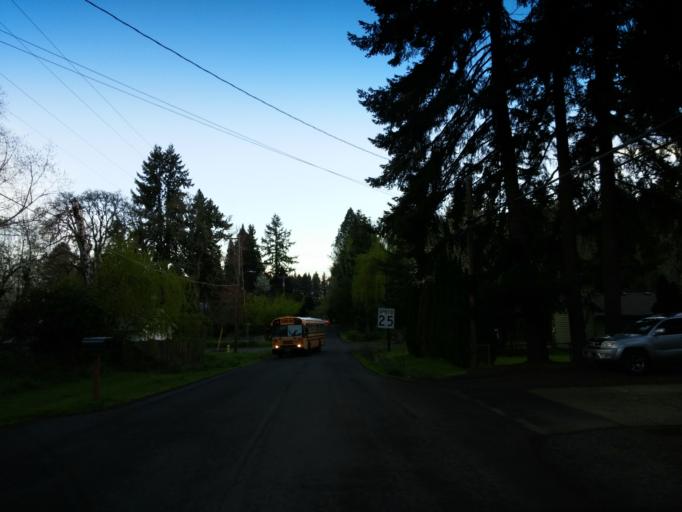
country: US
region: Oregon
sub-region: Washington County
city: Aloha
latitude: 45.5076
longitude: -122.8753
